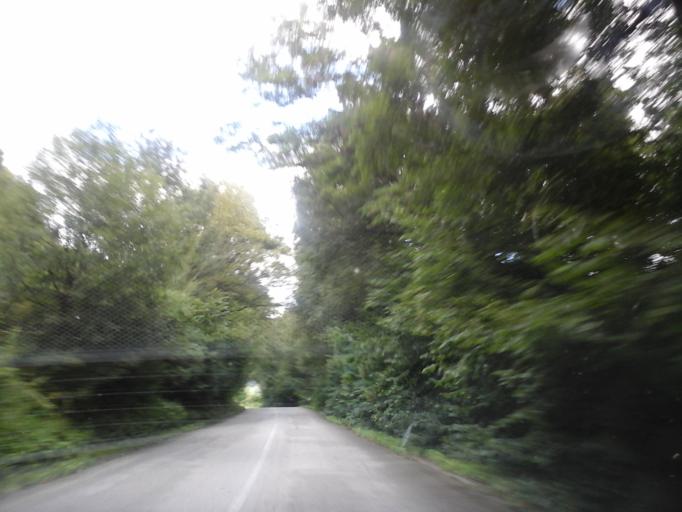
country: SK
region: Kosicky
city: Roznava
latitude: 48.5553
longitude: 20.4002
